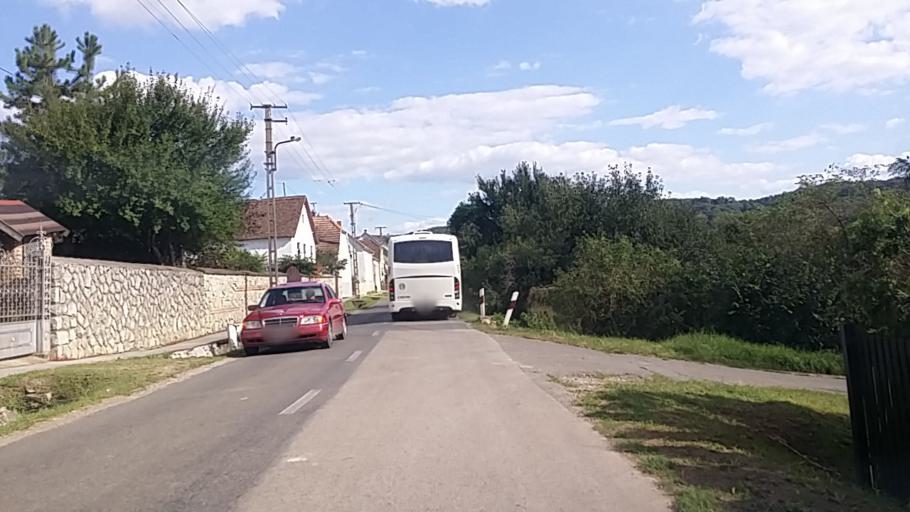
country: HU
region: Baranya
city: Sasd
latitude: 46.1453
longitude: 18.1134
